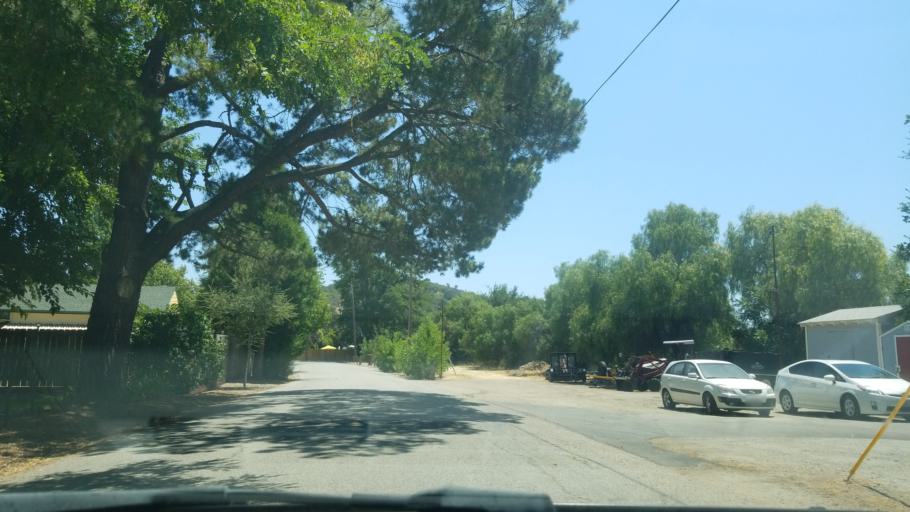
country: US
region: California
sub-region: San Luis Obispo County
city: Atascadero
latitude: 35.5028
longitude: -120.6642
